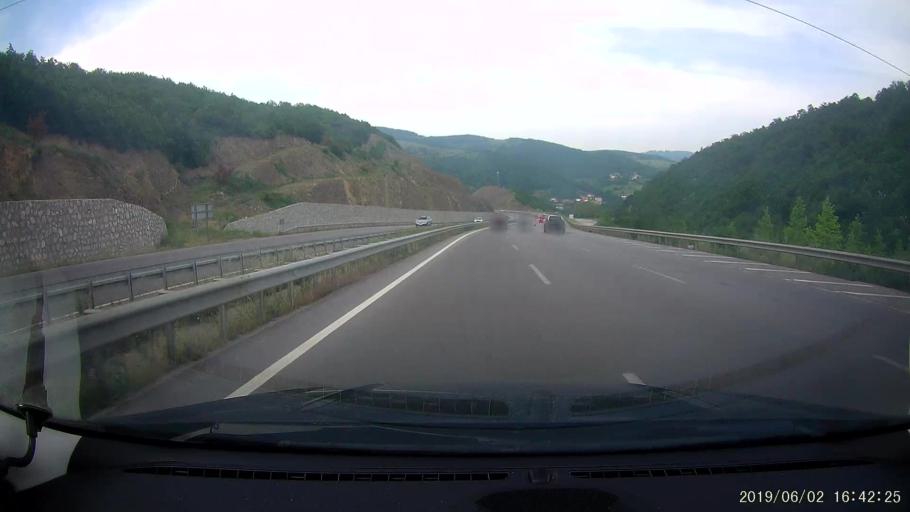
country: TR
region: Samsun
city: Kavak
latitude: 41.1186
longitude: 36.1315
